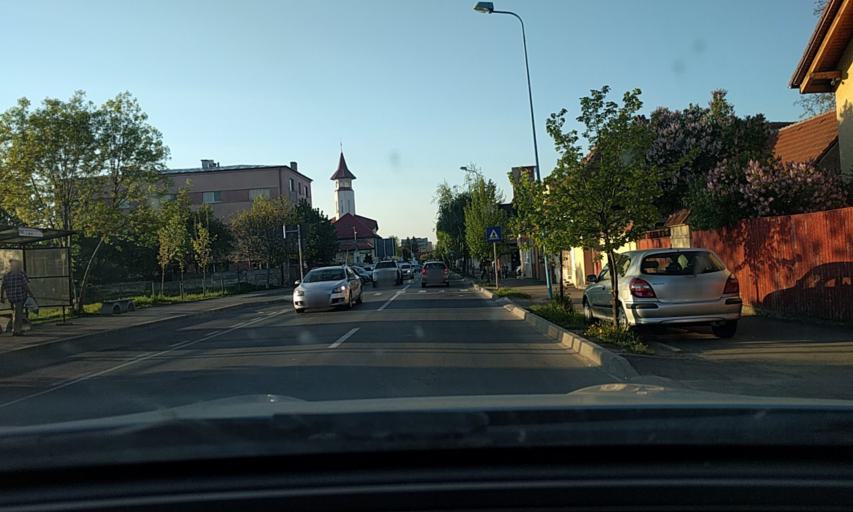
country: RO
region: Brasov
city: Brasov
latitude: 45.6642
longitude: 25.5781
